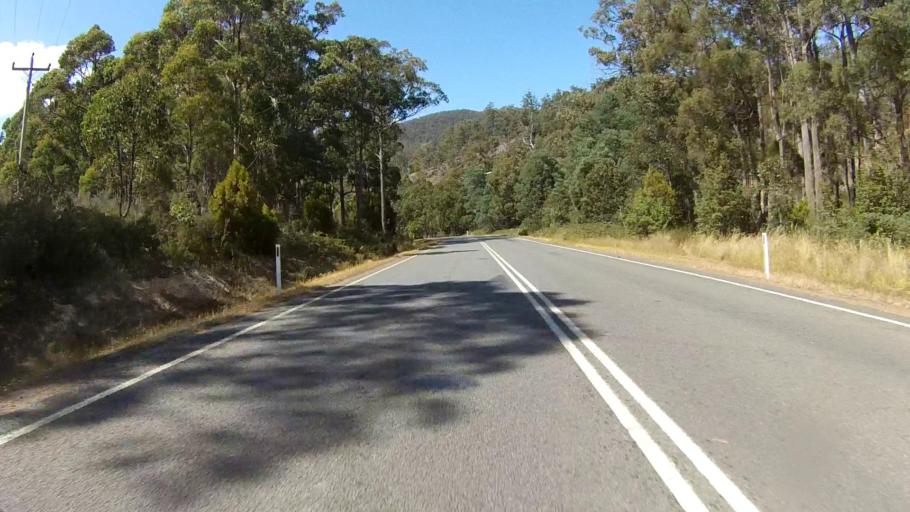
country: AU
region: Tasmania
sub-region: Derwent Valley
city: New Norfolk
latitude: -42.6819
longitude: 146.7316
